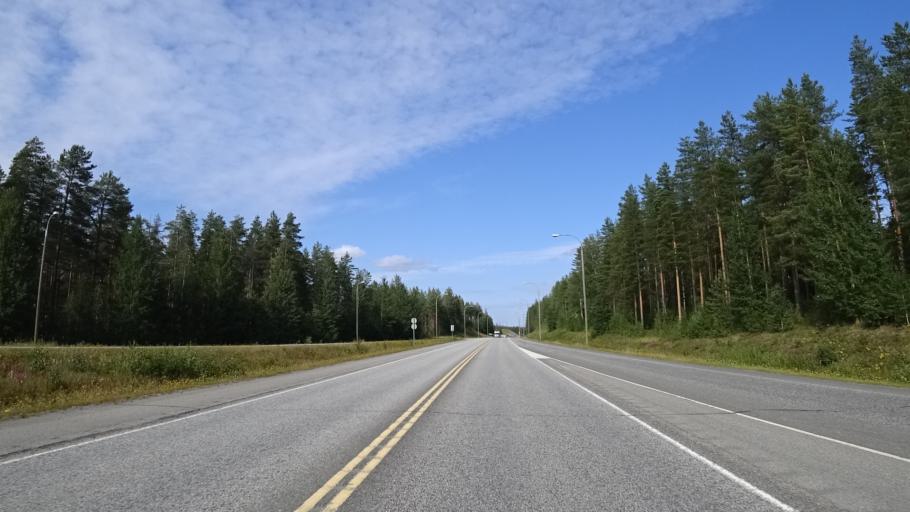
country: FI
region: North Karelia
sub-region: Joensuu
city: Joensuu
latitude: 62.6769
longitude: 29.7930
